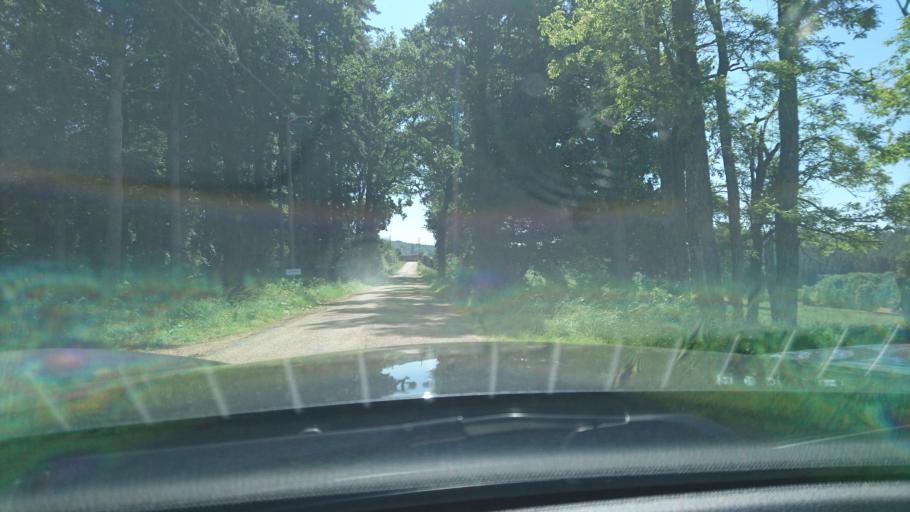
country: FR
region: Rhone-Alpes
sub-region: Departement de la Loire
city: Bussieres
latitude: 45.8573
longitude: 4.2445
